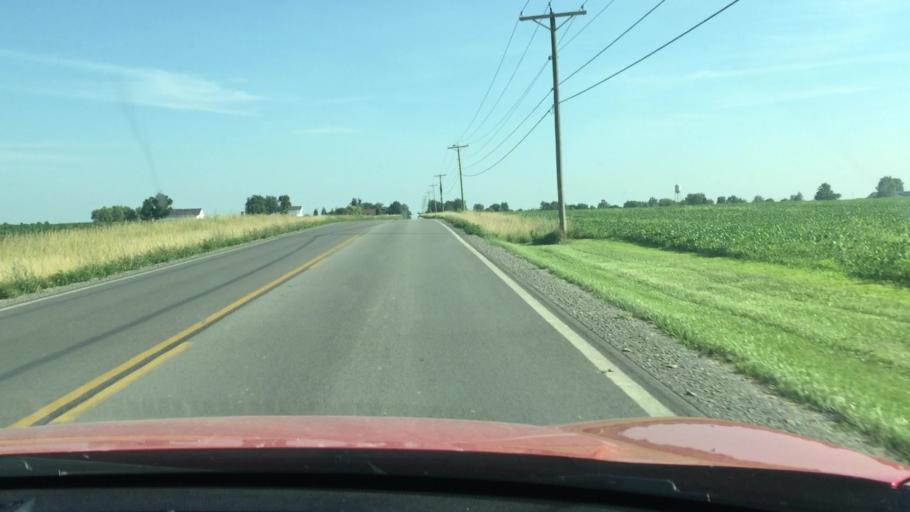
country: US
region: Ohio
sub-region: Hardin County
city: Ada
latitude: 40.7241
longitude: -83.8423
